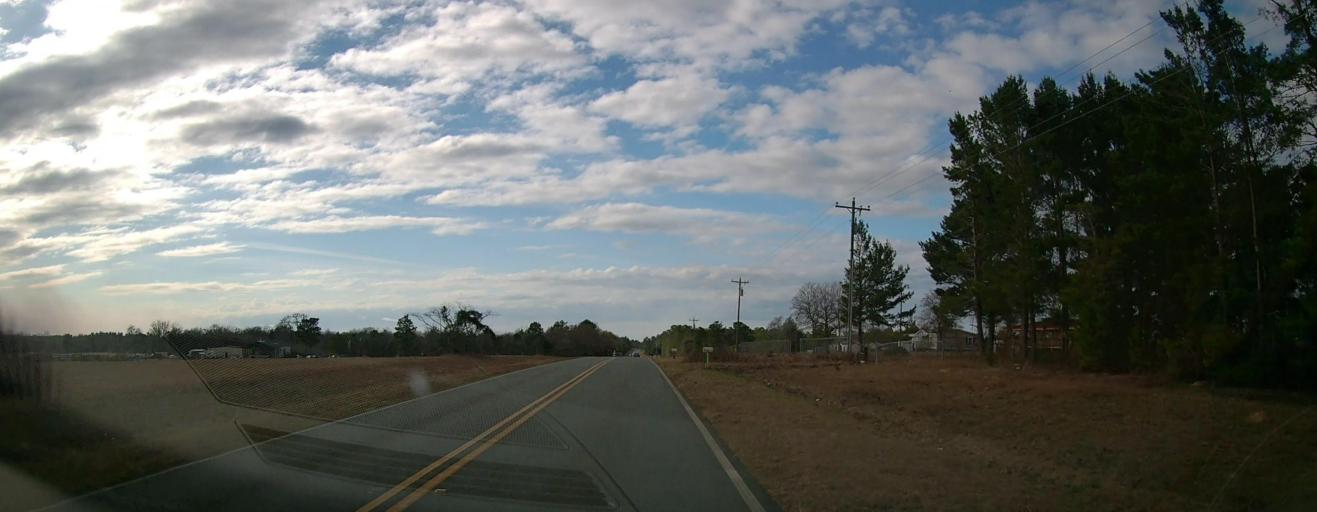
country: US
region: Georgia
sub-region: Marion County
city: Buena Vista
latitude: 32.4942
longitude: -84.5573
